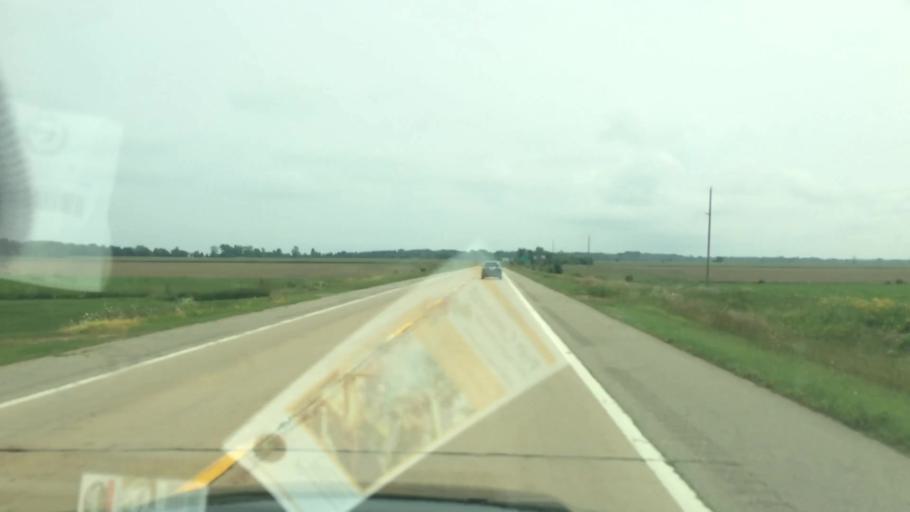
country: US
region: Michigan
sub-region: Huron County
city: Bad Axe
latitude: 44.0438
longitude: -82.8998
